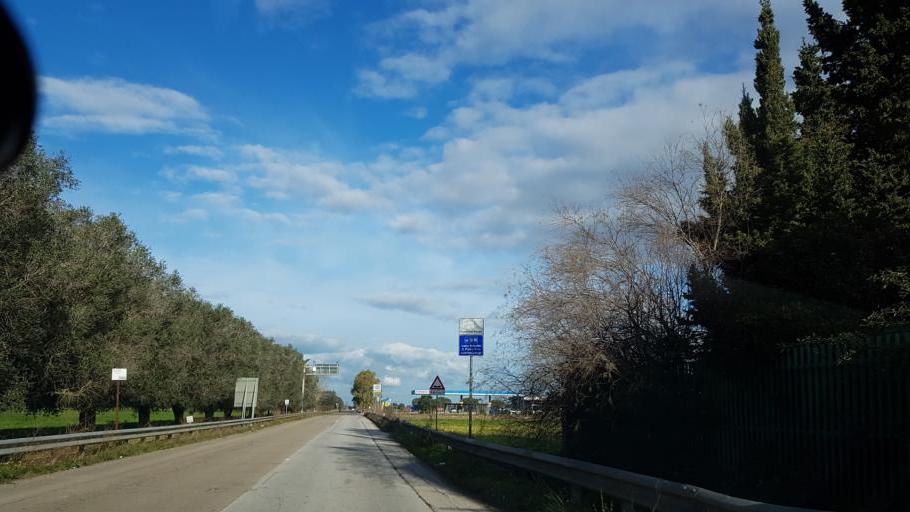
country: IT
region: Apulia
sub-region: Provincia di Brindisi
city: Tuturano
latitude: 40.5504
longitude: 17.9758
